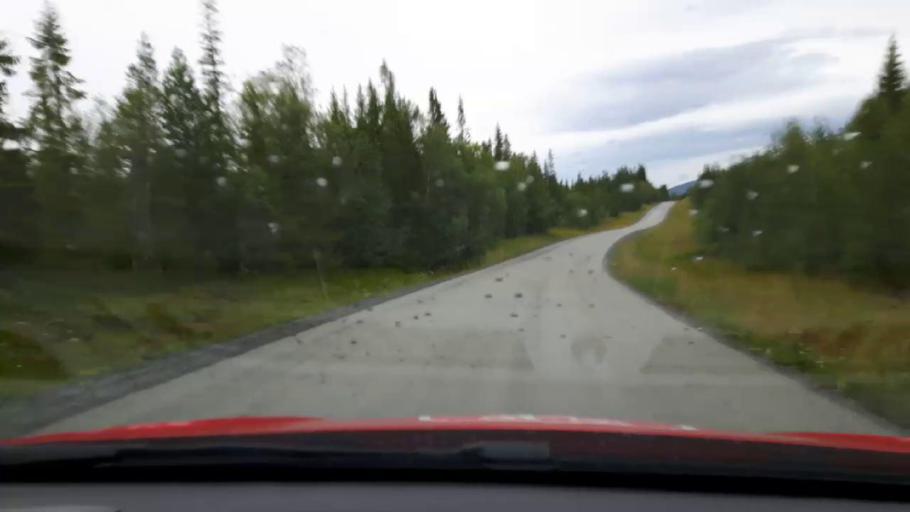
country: SE
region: Jaemtland
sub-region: Are Kommun
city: Are
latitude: 63.4523
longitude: 13.2073
